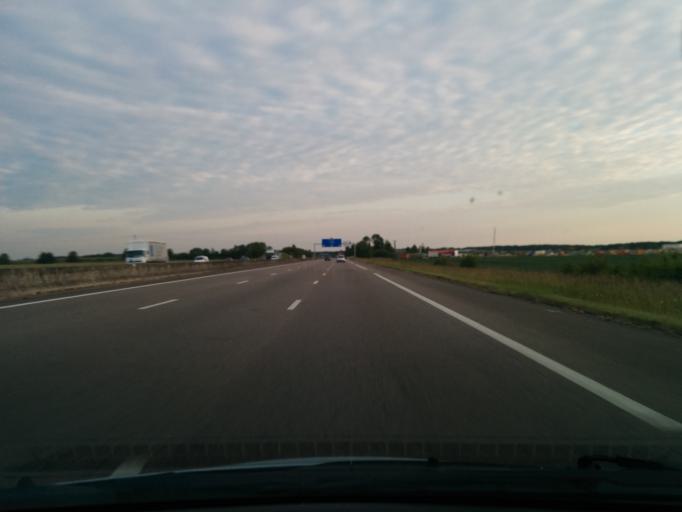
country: FR
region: Haute-Normandie
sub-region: Departement de l'Eure
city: Saint-Aubin-sur-Gaillon
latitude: 49.1306
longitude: 1.3194
